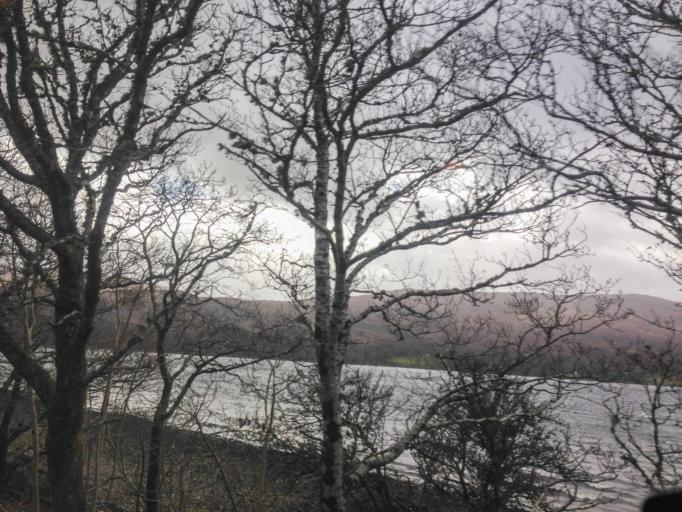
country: GB
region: Scotland
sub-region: Highland
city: Fort William
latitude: 56.8541
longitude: -5.1884
